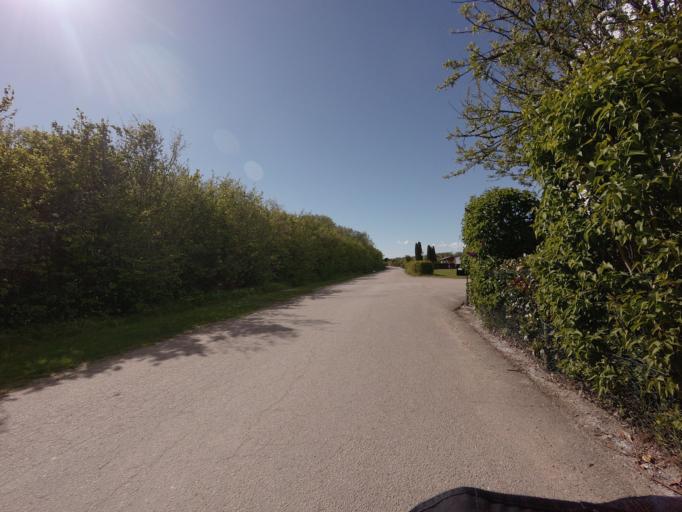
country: SE
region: Skane
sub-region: Landskrona
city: Landskrona
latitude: 55.8950
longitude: 12.8459
